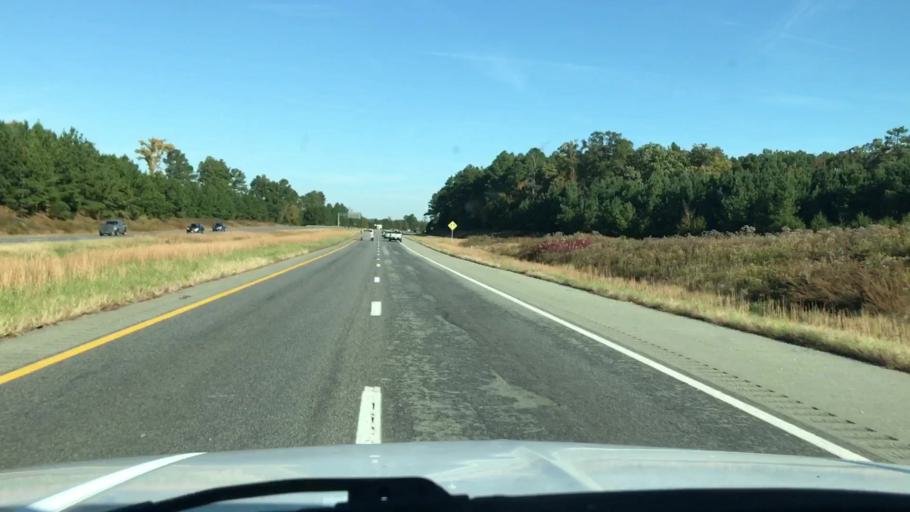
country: US
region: Virginia
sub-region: Henrico County
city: Short Pump
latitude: 37.6398
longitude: -77.6643
